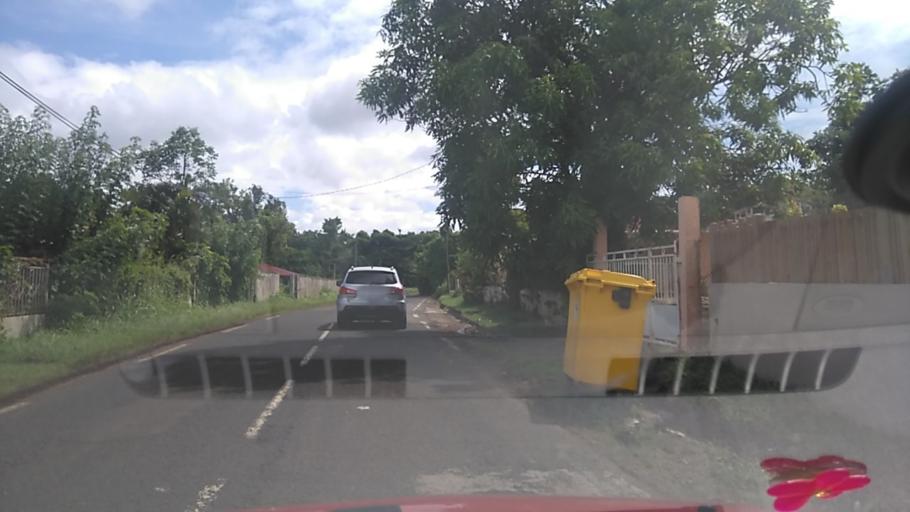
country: MQ
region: Martinique
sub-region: Martinique
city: Saint-Esprit
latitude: 14.5809
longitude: -60.9270
